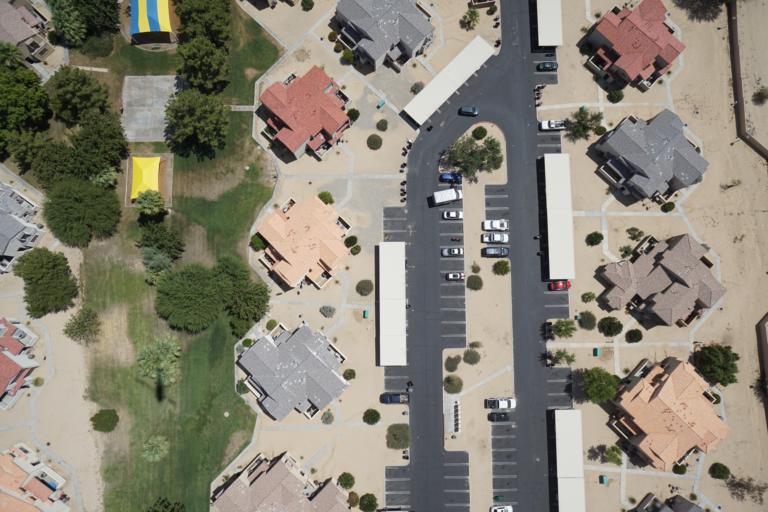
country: US
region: California
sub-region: San Bernardino County
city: Twentynine Palms
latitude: 34.1454
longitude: -116.0480
